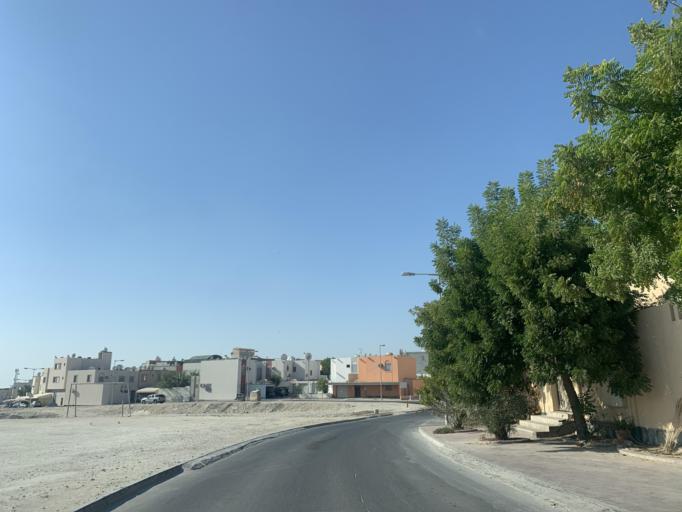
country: BH
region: Central Governorate
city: Madinat Hamad
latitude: 26.0979
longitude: 50.5078
